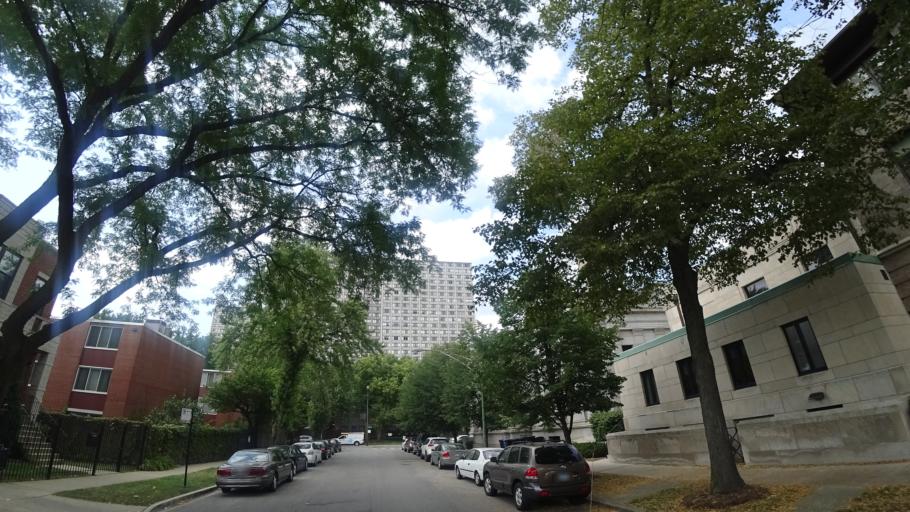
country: US
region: Illinois
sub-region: Cook County
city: Chicago
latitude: 41.8055
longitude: -87.5906
